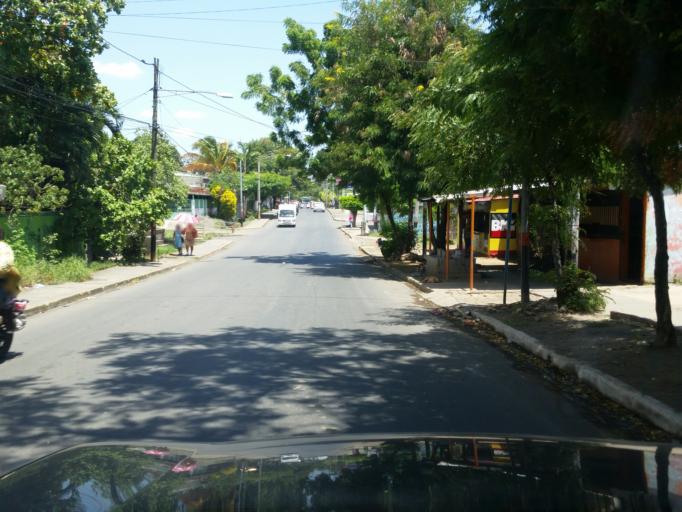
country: NI
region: Managua
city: Managua
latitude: 12.1233
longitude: -86.2109
